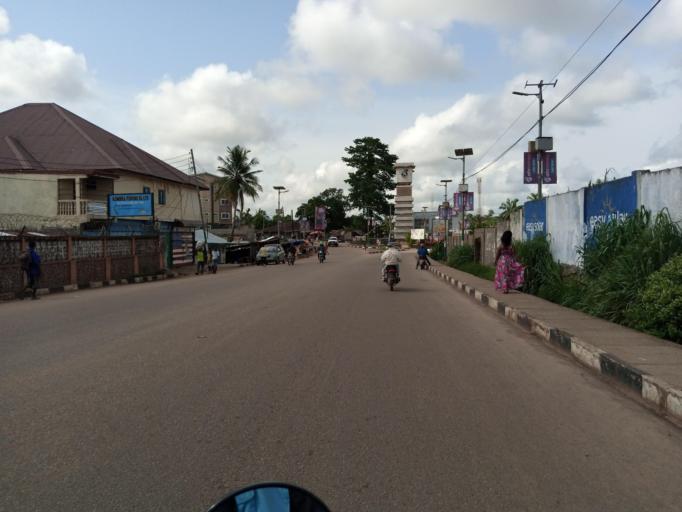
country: SL
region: Southern Province
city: Bo
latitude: 7.9609
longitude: -11.7399
